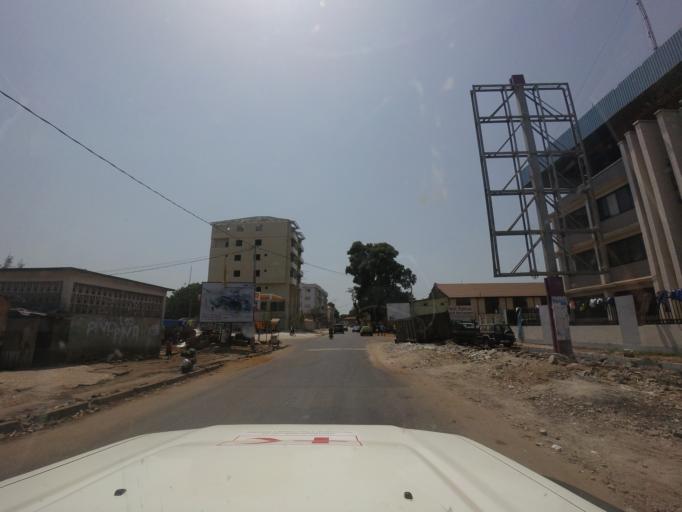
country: GN
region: Conakry
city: Camayenne
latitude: 9.5179
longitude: -13.7016
